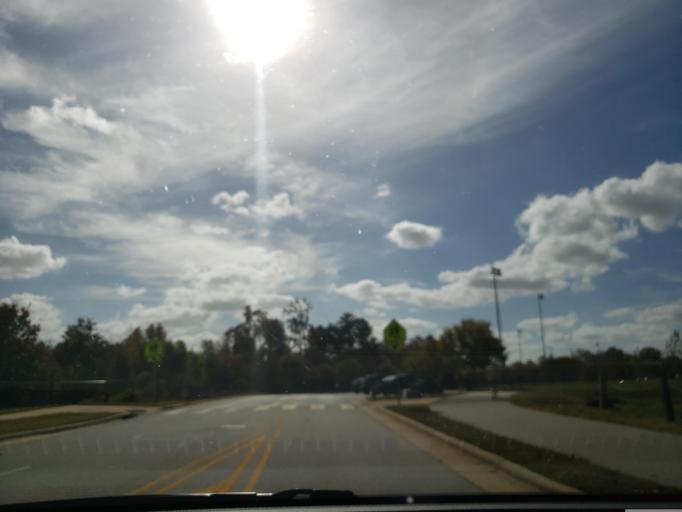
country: US
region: North Carolina
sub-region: Wake County
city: Apex
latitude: 35.7389
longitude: -78.8467
